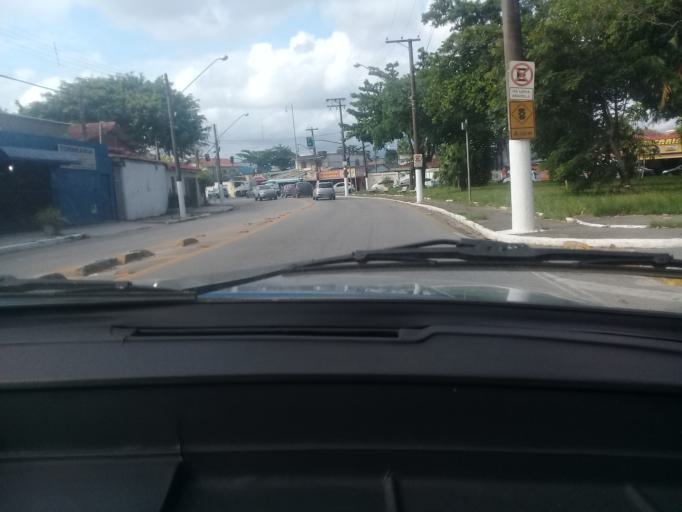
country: BR
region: Sao Paulo
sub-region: Guaruja
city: Guaruja
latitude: -23.9972
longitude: -46.2742
